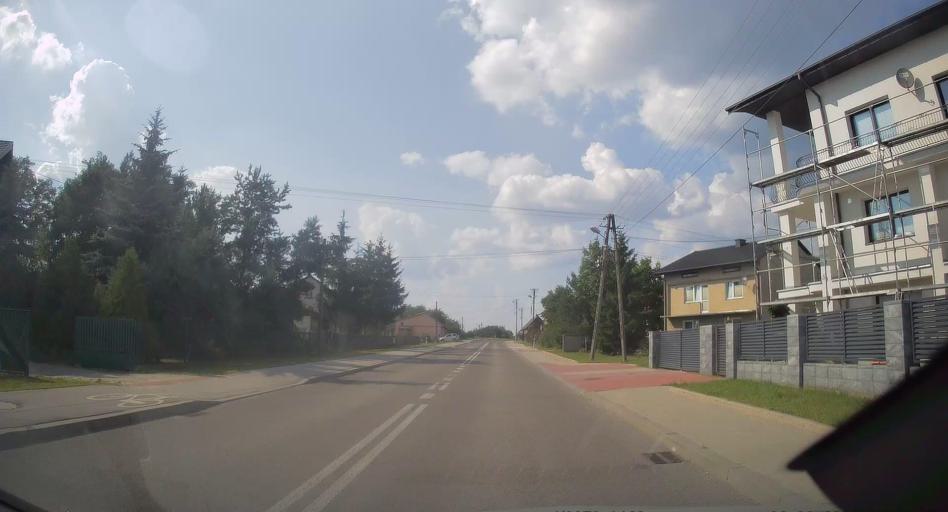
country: PL
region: Swietokrzyskie
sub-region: Powiat konecki
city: Radoszyce
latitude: 51.0639
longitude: 20.2740
